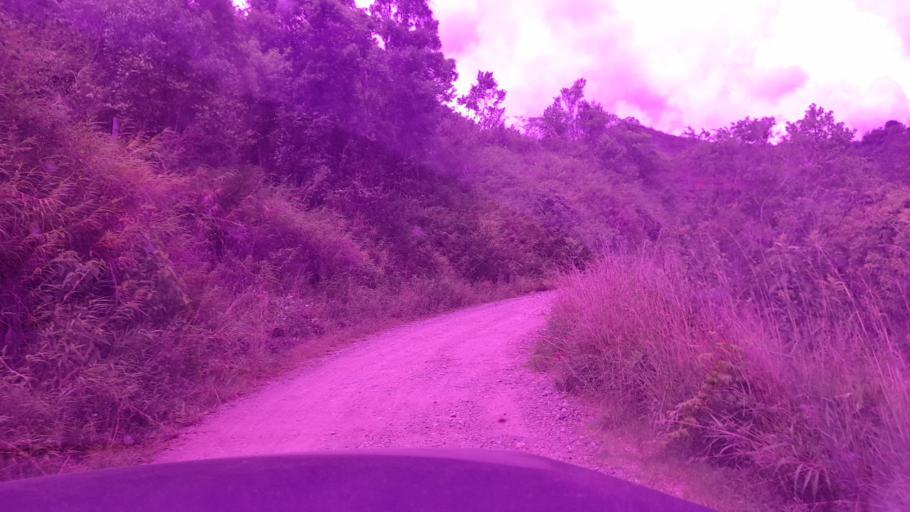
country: CO
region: Valle del Cauca
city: Andalucia
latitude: 4.1717
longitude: -76.1232
